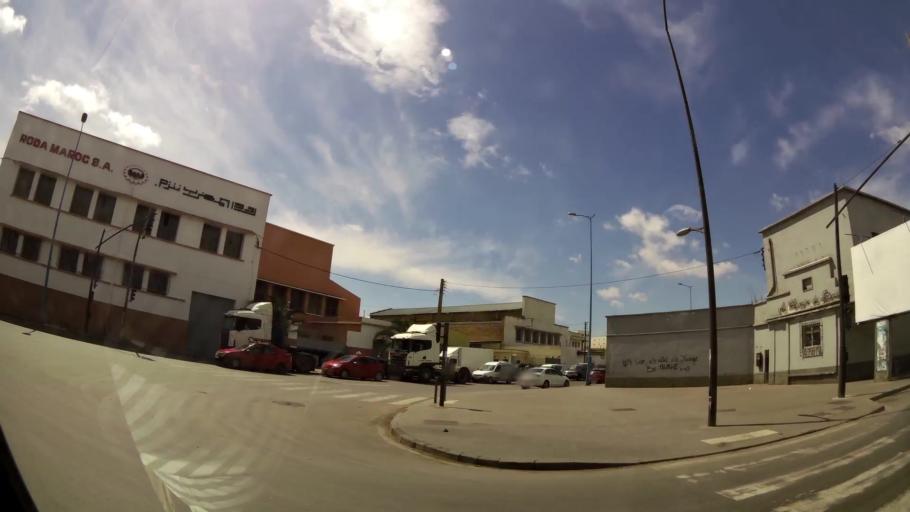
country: MA
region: Grand Casablanca
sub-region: Casablanca
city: Casablanca
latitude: 33.6040
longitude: -7.5423
